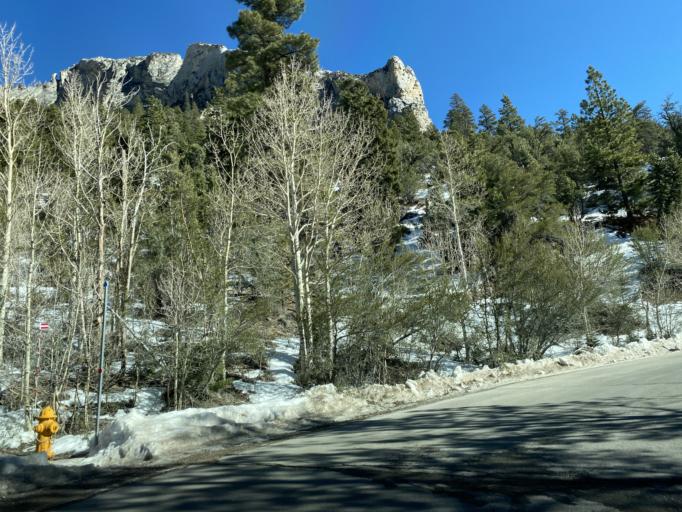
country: US
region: Nevada
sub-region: Nye County
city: Pahrump
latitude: 36.2675
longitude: -115.6579
